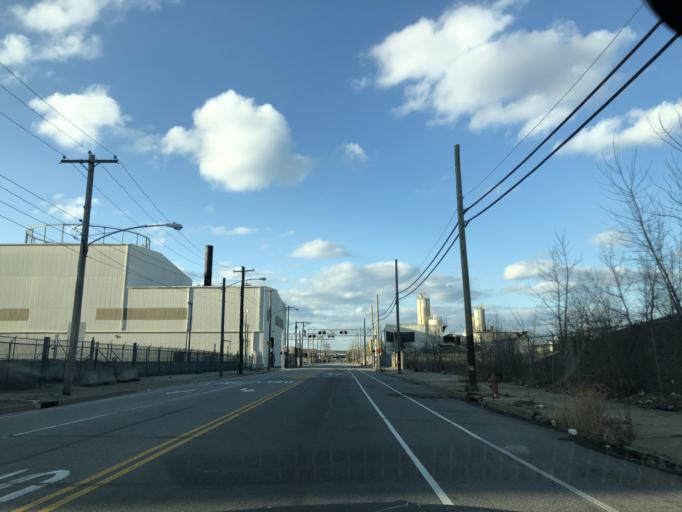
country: US
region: New Jersey
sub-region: Camden County
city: Pennsauken
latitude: 39.9829
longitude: -75.0841
